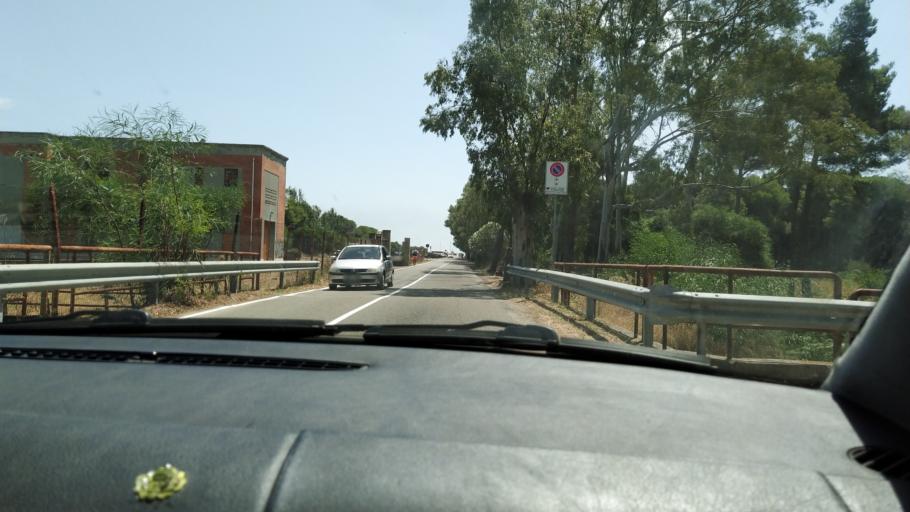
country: IT
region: Basilicate
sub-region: Provincia di Matera
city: Marconia
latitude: 40.3223
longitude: 16.7963
